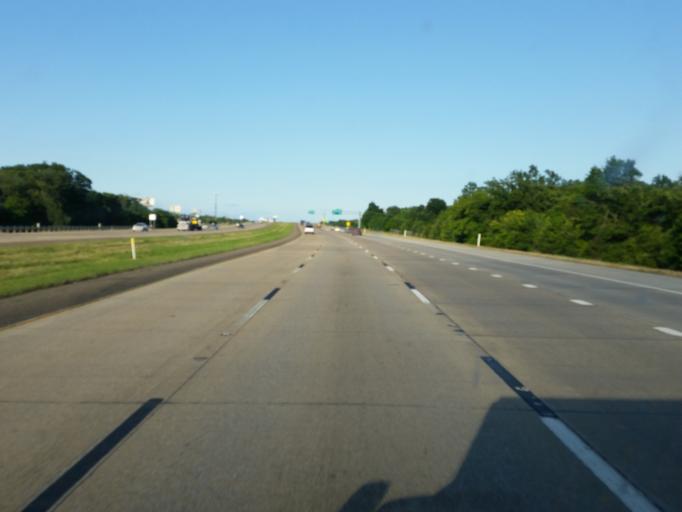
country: US
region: Texas
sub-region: Dallas County
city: Balch Springs
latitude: 32.7018
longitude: -96.6126
